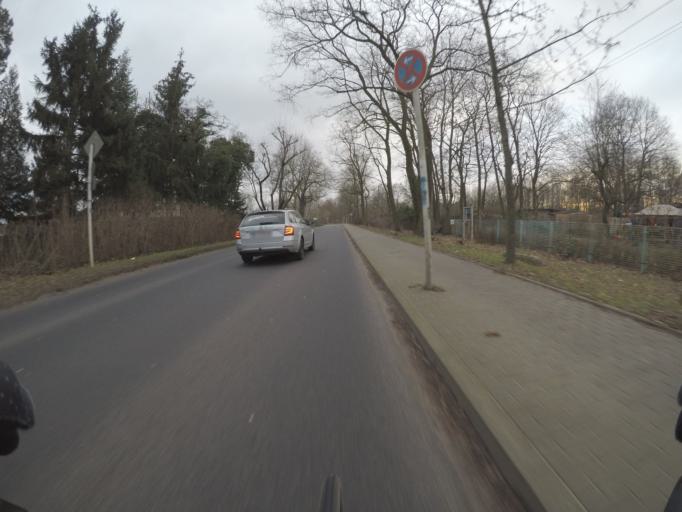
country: DE
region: Berlin
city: Karlshorst
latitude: 52.4741
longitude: 13.5460
